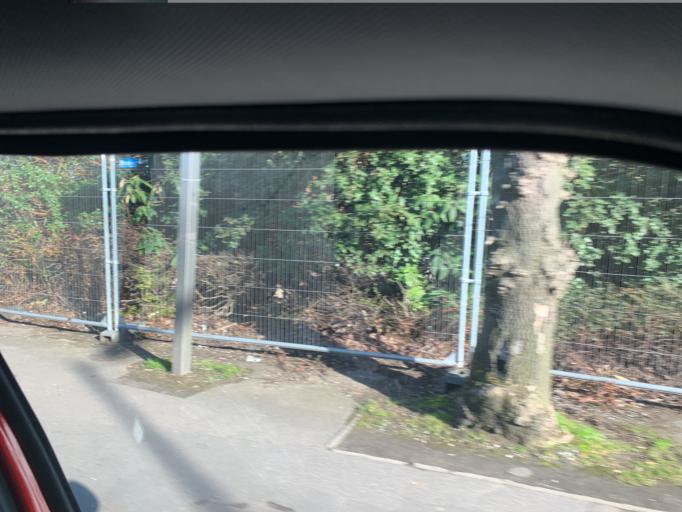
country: GB
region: England
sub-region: Buckinghamshire
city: Farnham Royal
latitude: 51.5170
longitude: -0.6245
